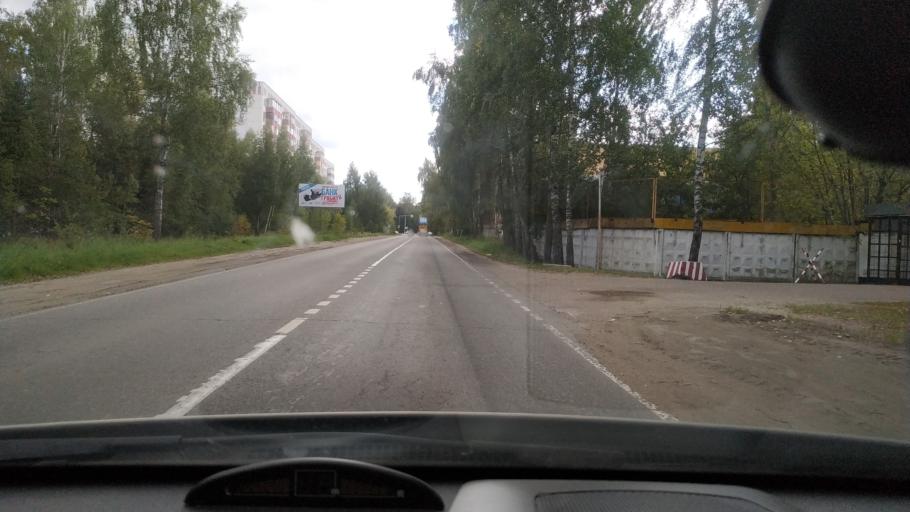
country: RU
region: Moskovskaya
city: Chornaya
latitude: 55.7623
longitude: 38.0740
